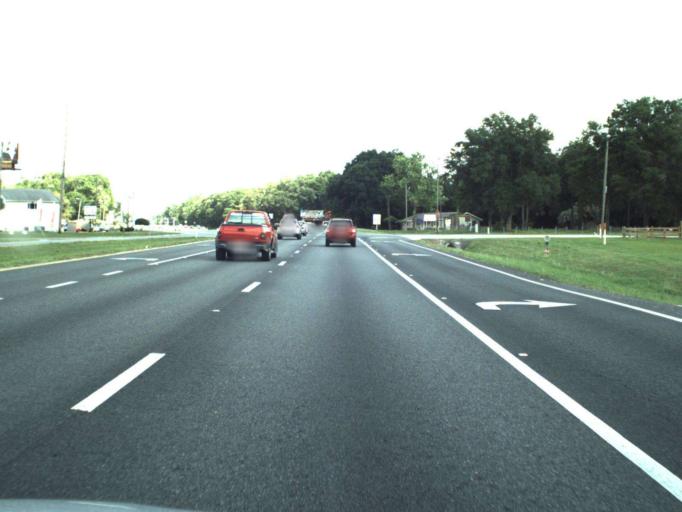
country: US
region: Florida
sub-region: Marion County
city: Silver Springs Shores
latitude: 29.1428
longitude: -82.0624
